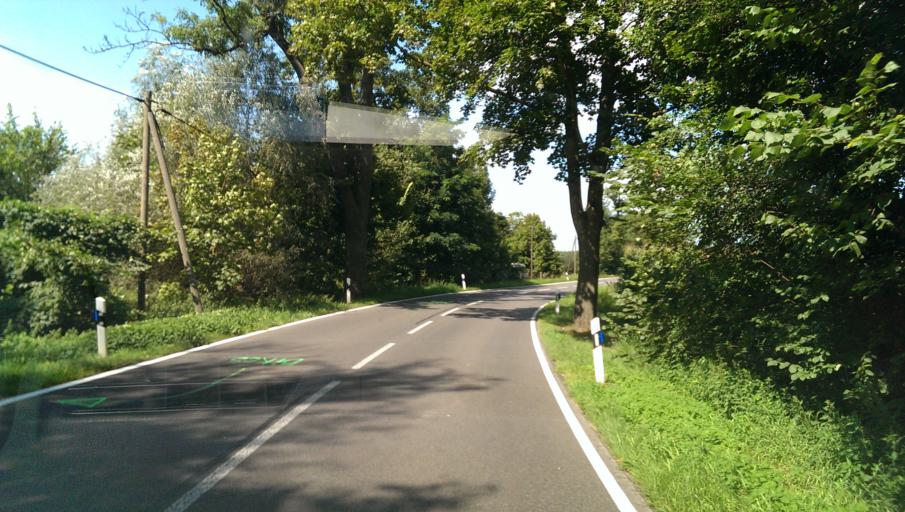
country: DE
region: Brandenburg
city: Trebbin
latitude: 52.2531
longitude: 13.2067
